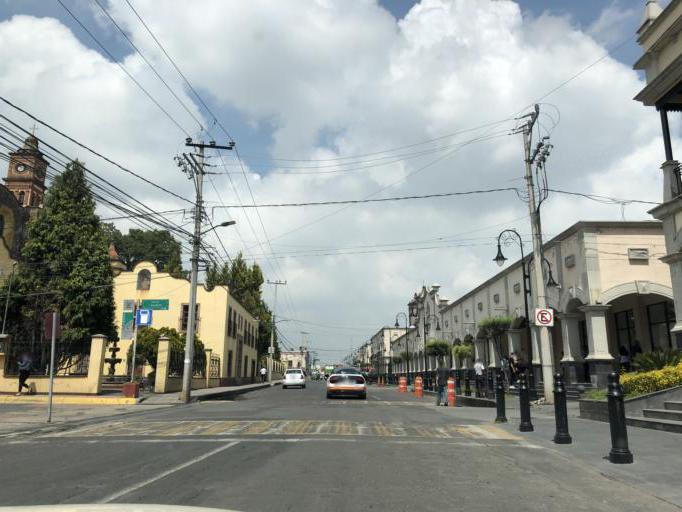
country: MX
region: Morelos
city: Lerma de Villada
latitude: 19.2864
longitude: -99.5101
